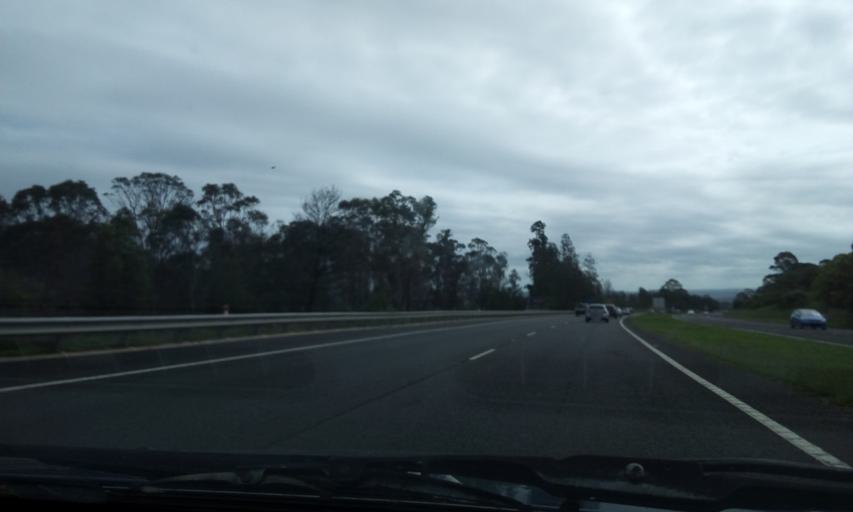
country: AU
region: New South Wales
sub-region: Camden
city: Narellan Vale
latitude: -34.0635
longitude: 150.7229
